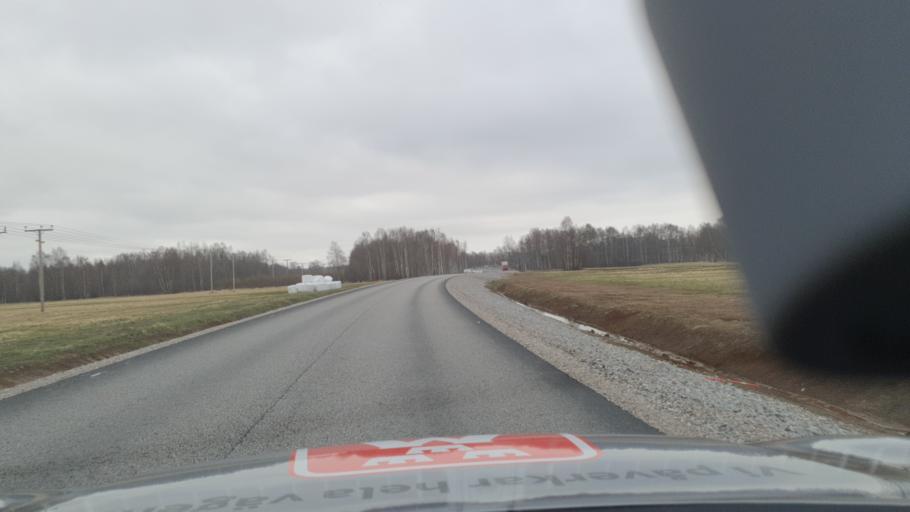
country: SE
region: Norrbotten
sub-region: Kalix Kommun
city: Rolfs
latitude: 65.8829
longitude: 23.0632
